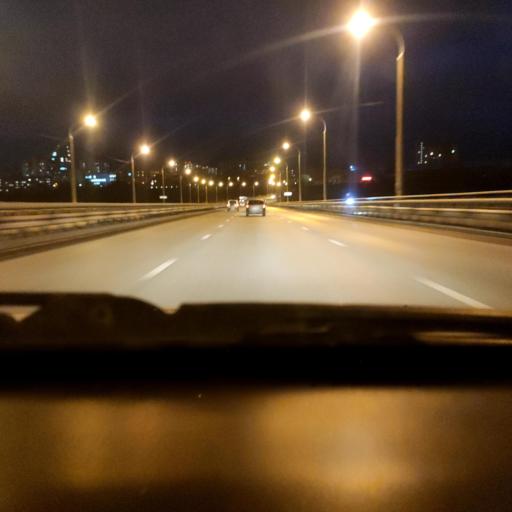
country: RU
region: Perm
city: Perm
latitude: 57.9847
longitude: 56.2309
